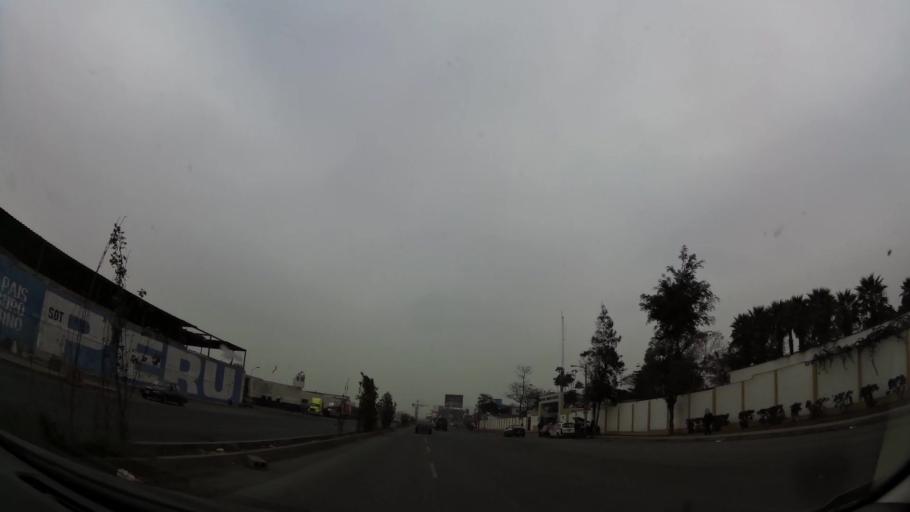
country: PE
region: Lima
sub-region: Lima
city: Vitarte
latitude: -12.0467
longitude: -76.9451
